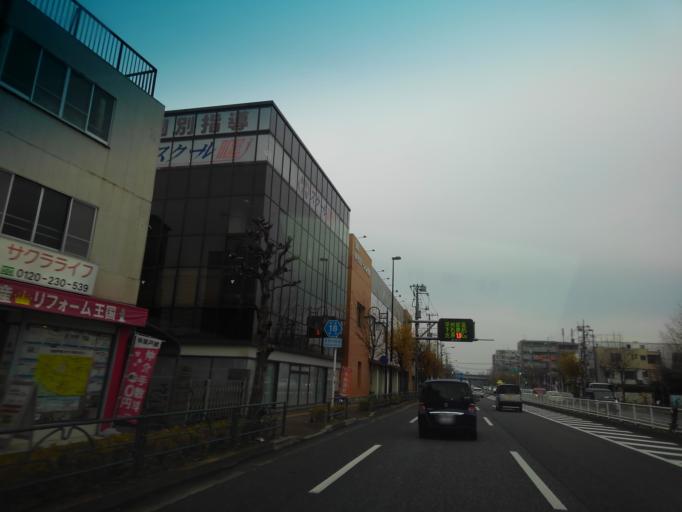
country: JP
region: Tokyo
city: Kokubunji
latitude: 35.6611
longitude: 139.4577
